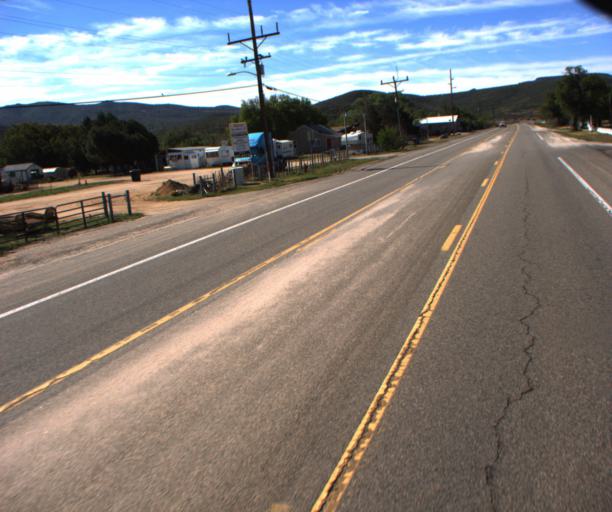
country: US
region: Arizona
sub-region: Yavapai County
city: Congress
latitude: 34.2685
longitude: -112.7273
